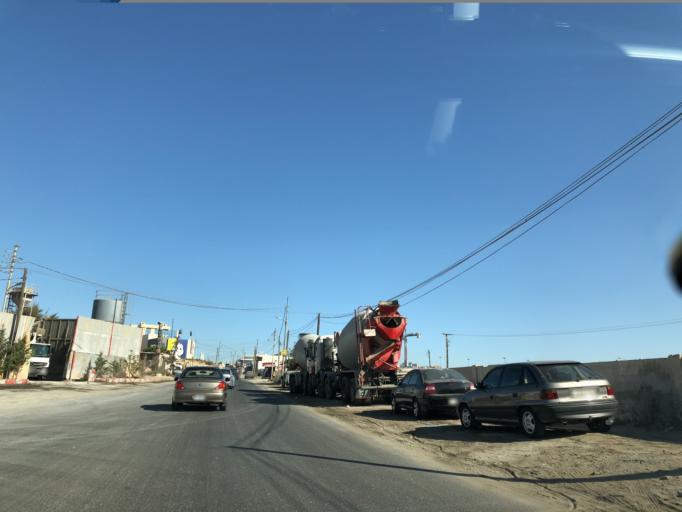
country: JO
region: Amman
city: Wadi as Sir
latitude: 31.9384
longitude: 35.8487
